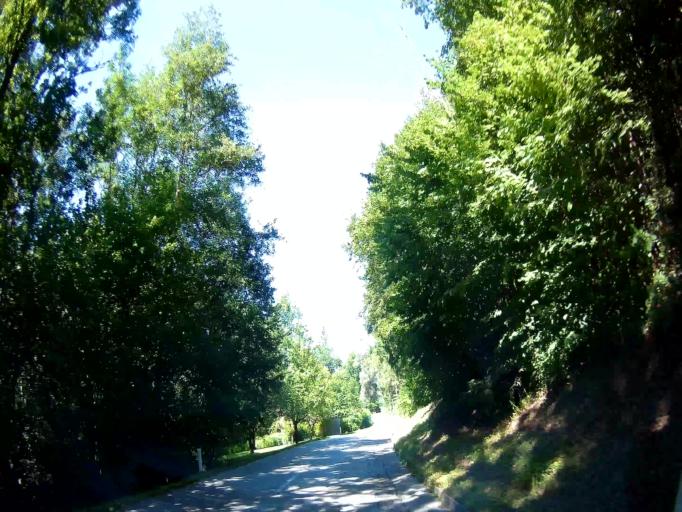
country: AT
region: Carinthia
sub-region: Politischer Bezirk Klagenfurt Land
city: Grafenstein
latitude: 46.6034
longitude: 14.4414
